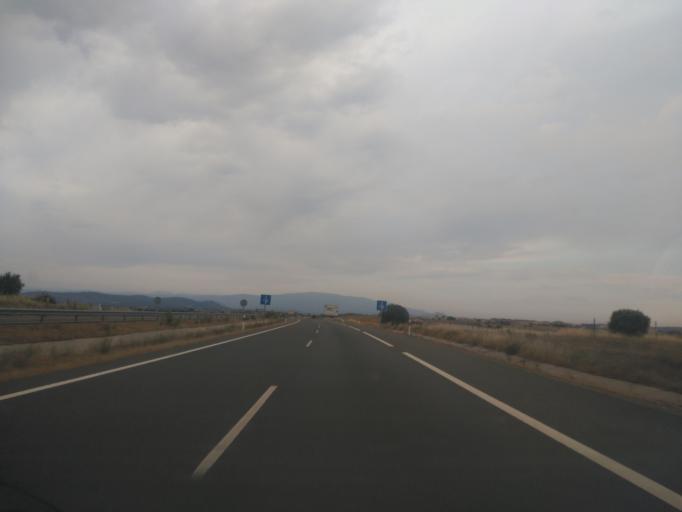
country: ES
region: Castille and Leon
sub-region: Provincia de Salamanca
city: Guijuelo
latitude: 40.5809
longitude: -5.6581
